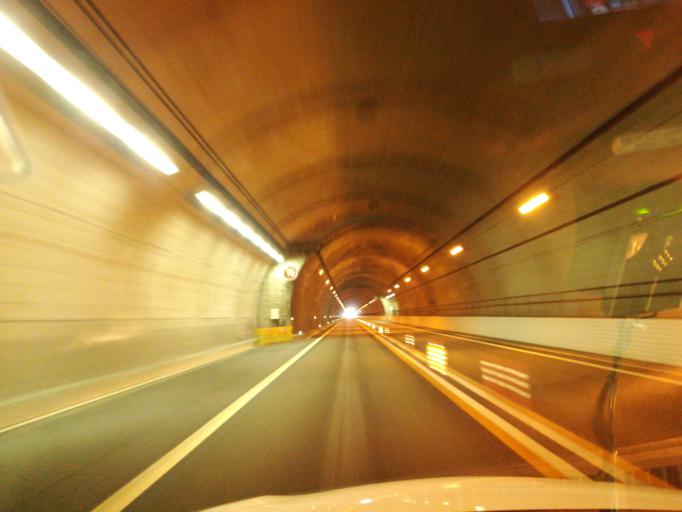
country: JP
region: Tokushima
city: Ikedacho
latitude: 34.0235
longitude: 133.7915
